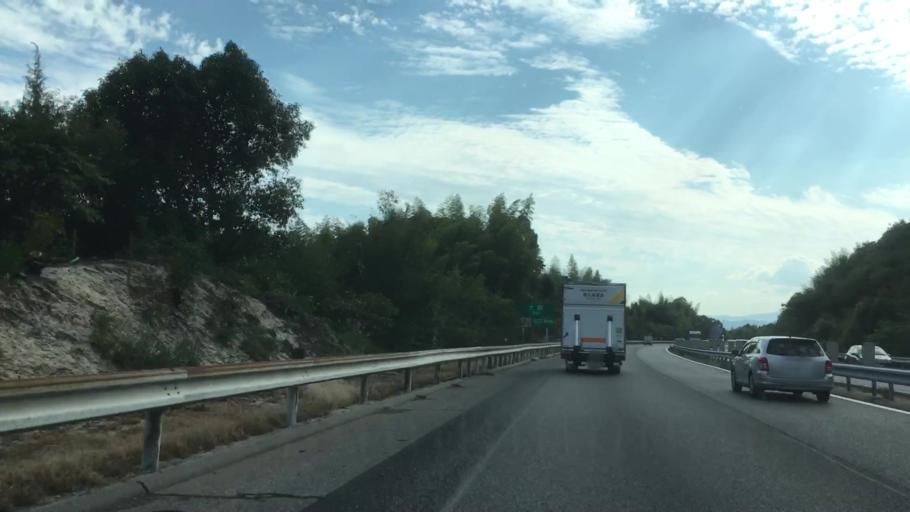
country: JP
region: Hiroshima
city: Ono-hara
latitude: 34.3080
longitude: 132.2798
